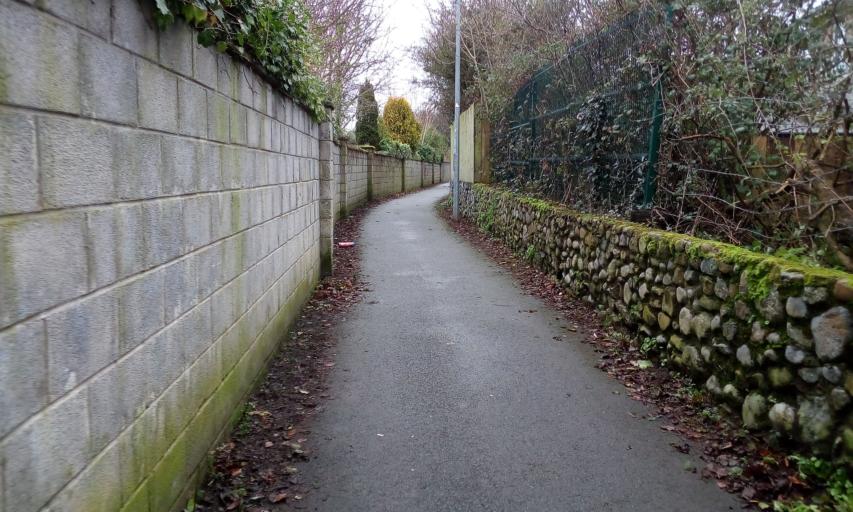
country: IE
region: Leinster
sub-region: Kilkenny
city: Kilkenny
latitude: 52.6437
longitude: -7.2568
